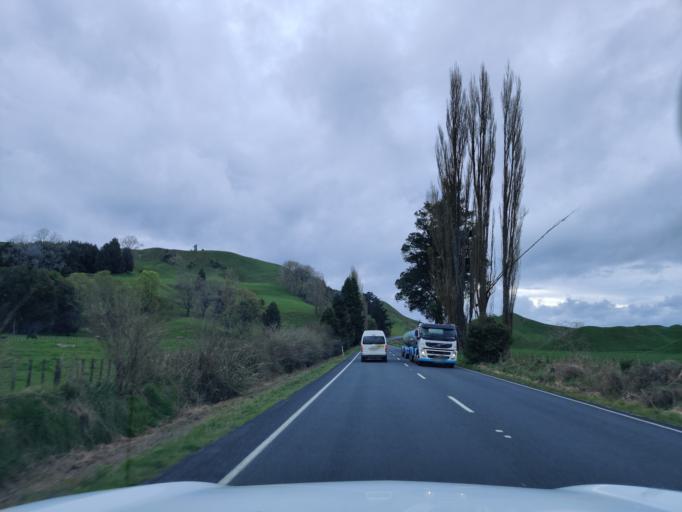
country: NZ
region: Waikato
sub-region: Otorohanga District
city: Otorohanga
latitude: -38.4725
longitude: 175.1732
